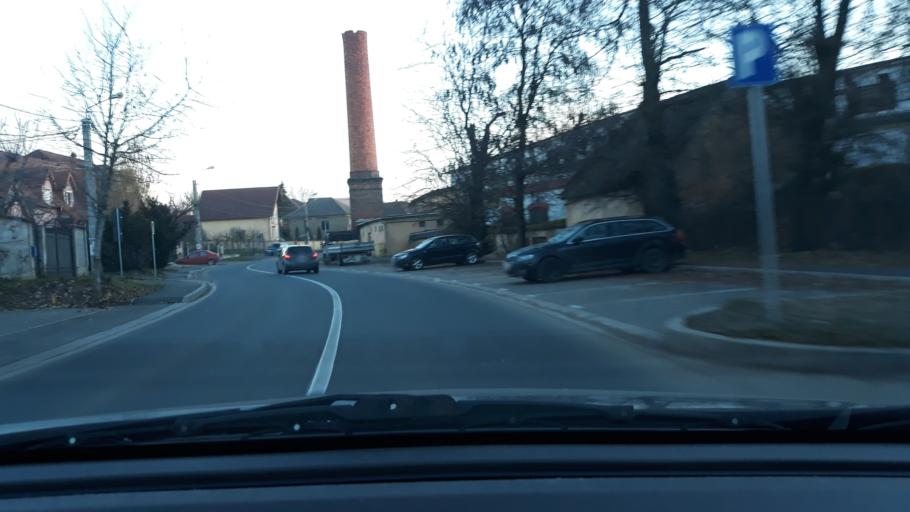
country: RO
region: Bihor
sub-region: Comuna Biharea
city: Oradea
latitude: 47.0822
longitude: 21.9276
